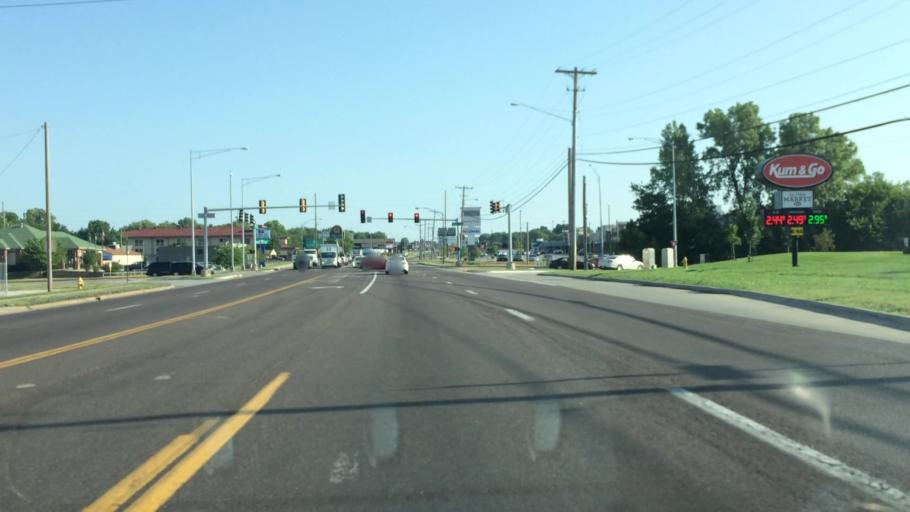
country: US
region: Missouri
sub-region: Greene County
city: Springfield
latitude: 37.1655
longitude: -93.2953
